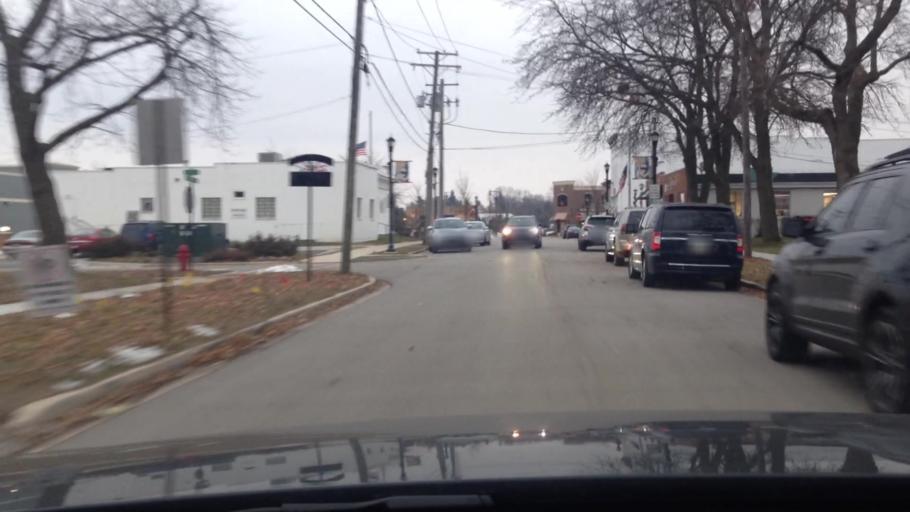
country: US
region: Illinois
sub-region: McHenry County
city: Huntley
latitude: 42.1695
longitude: -88.4263
